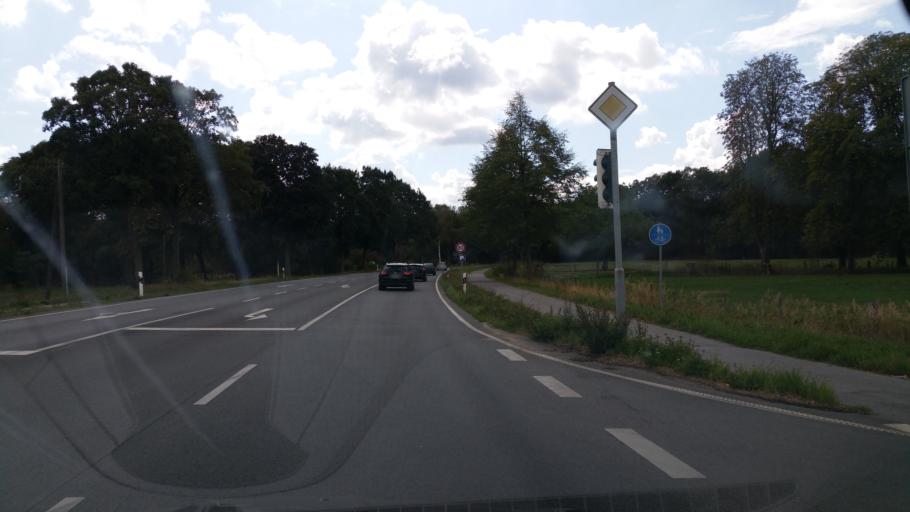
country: DE
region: North Rhine-Westphalia
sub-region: Regierungsbezirk Dusseldorf
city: Hamminkeln
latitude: 51.7290
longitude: 6.6002
